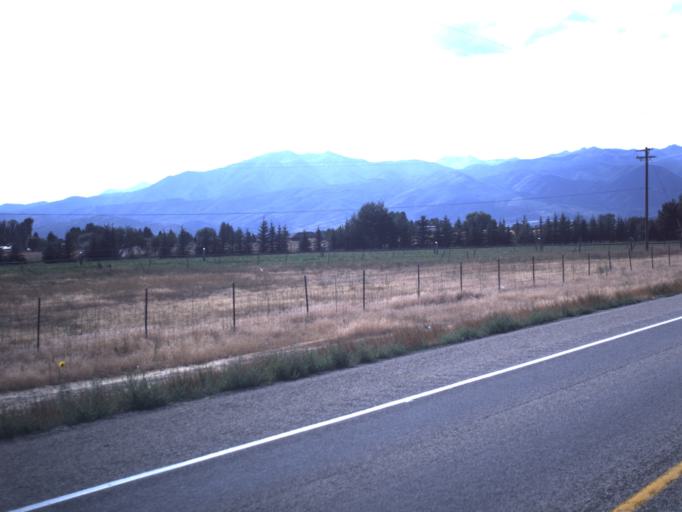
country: US
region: Utah
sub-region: Wasatch County
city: Heber
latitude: 40.4673
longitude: -111.3871
